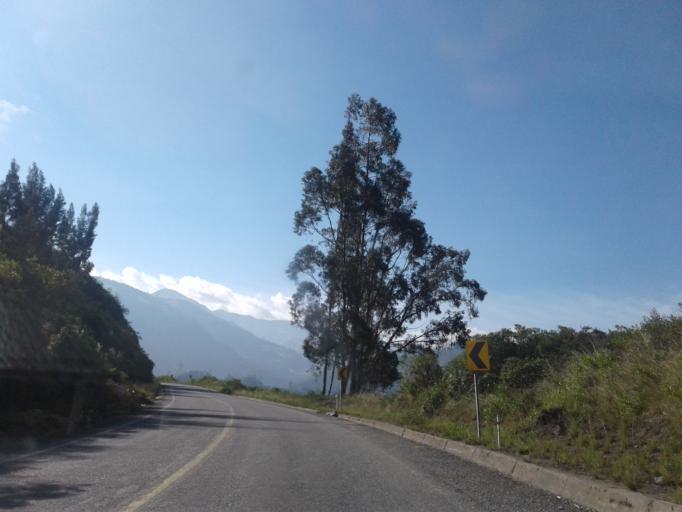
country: EC
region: Chimborazo
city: Guano
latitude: -1.5144
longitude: -78.5192
